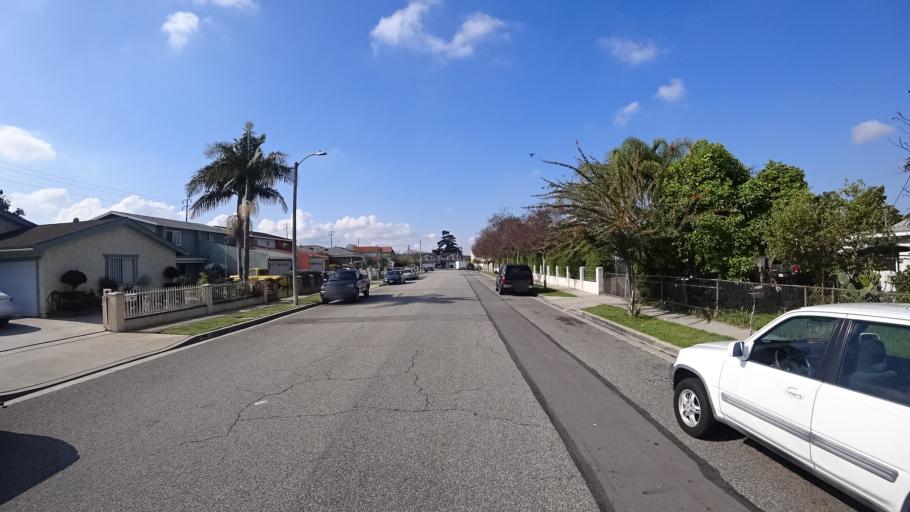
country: US
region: California
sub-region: Los Angeles County
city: Baldwin Park
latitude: 34.0763
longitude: -117.9625
